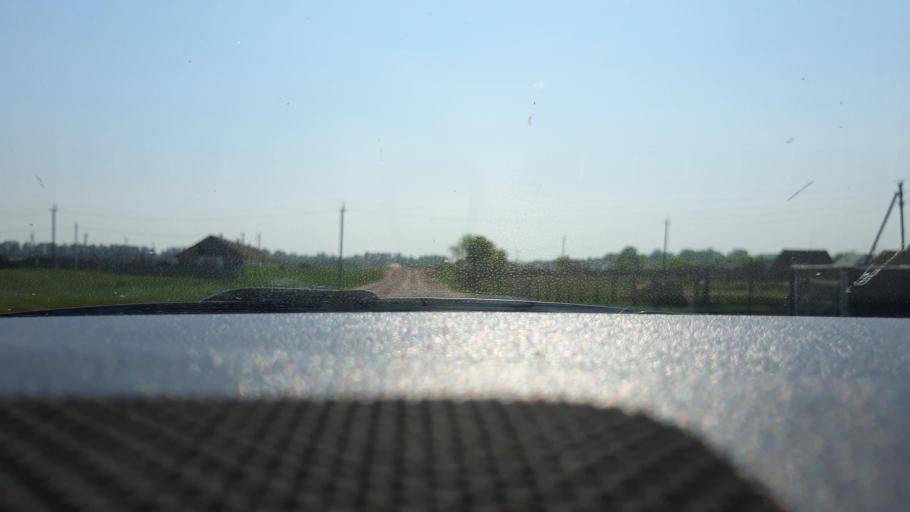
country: RU
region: Bashkortostan
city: Chishmy
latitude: 54.4457
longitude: 55.3174
